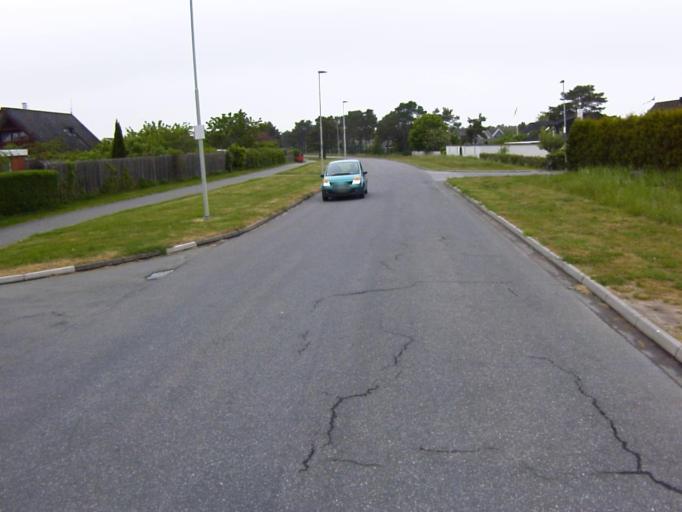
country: SE
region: Skane
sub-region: Kristianstads Kommun
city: Ahus
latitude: 55.9349
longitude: 14.2843
